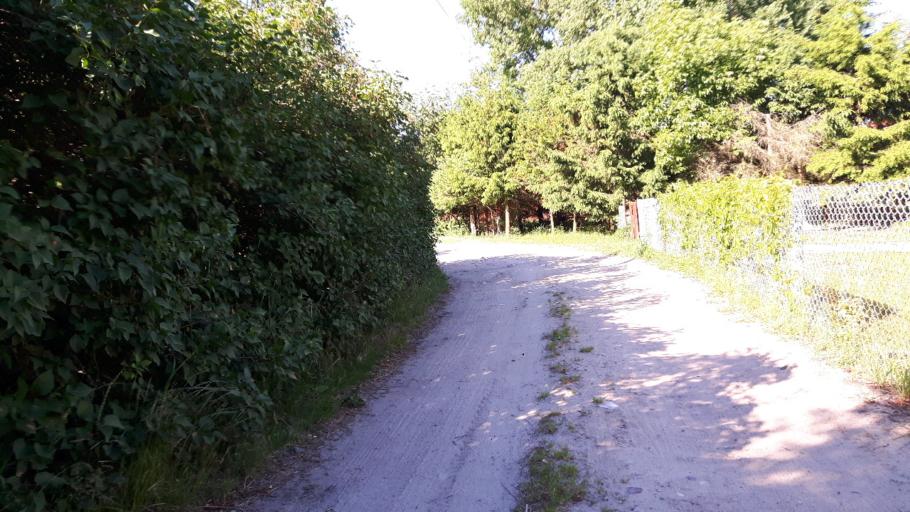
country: PL
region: Pomeranian Voivodeship
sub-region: Powiat leborski
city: Leba
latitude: 54.7205
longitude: 17.5242
